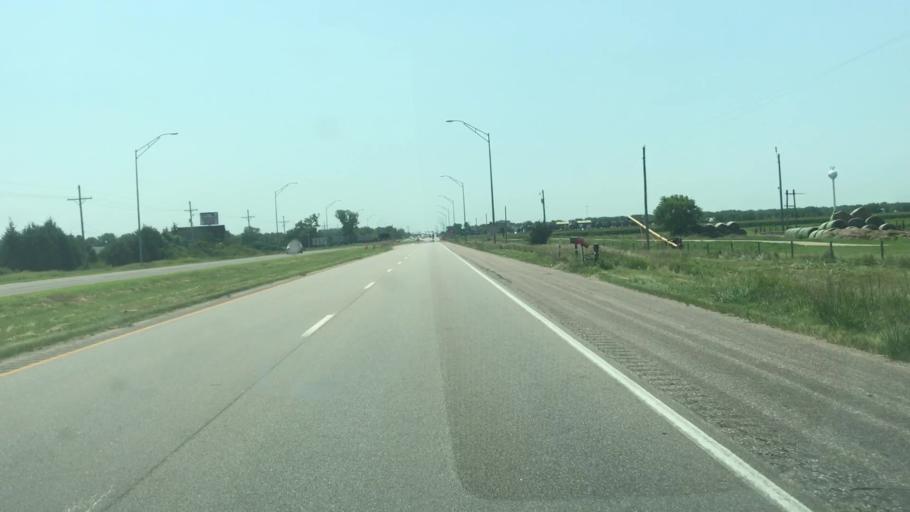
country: US
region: Nebraska
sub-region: Hall County
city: Grand Island
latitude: 40.8399
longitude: -98.3787
